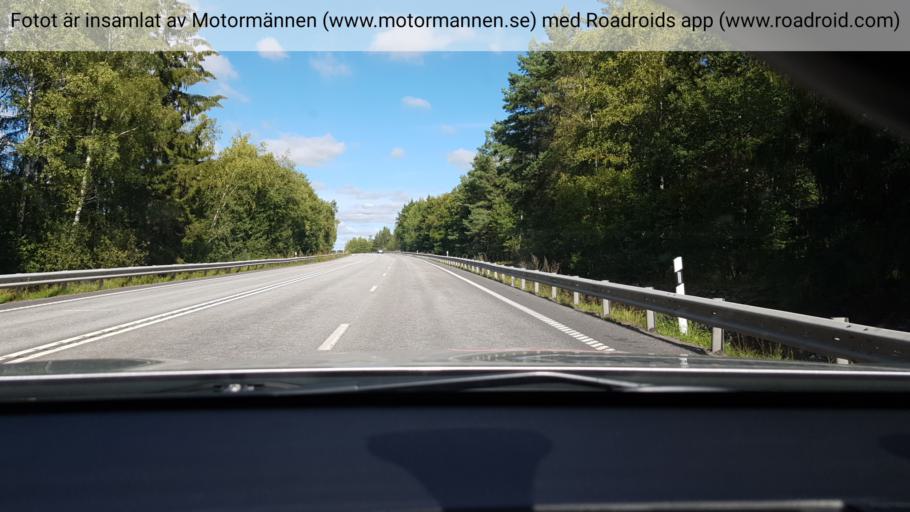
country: SE
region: Stockholm
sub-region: Lidingo
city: Brevik
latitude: 59.4370
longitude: 18.2204
